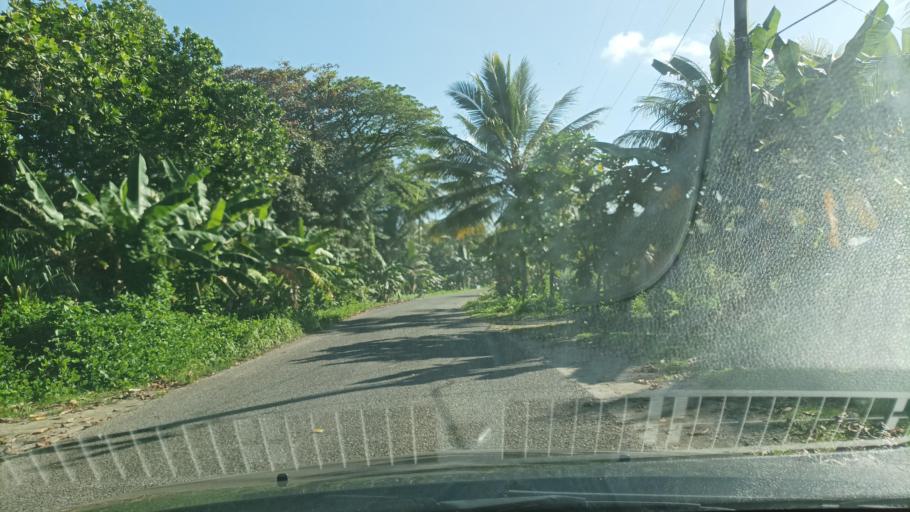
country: FM
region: Kosrae
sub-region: Malem Municipality
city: Malem
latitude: 5.2902
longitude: 163.0286
